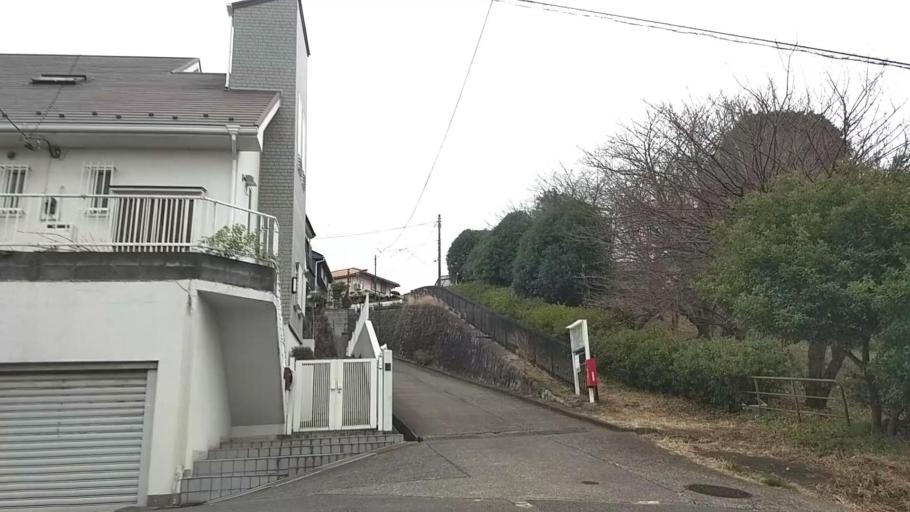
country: JP
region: Tokyo
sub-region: Machida-shi
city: Machida
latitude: 35.5607
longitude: 139.4441
